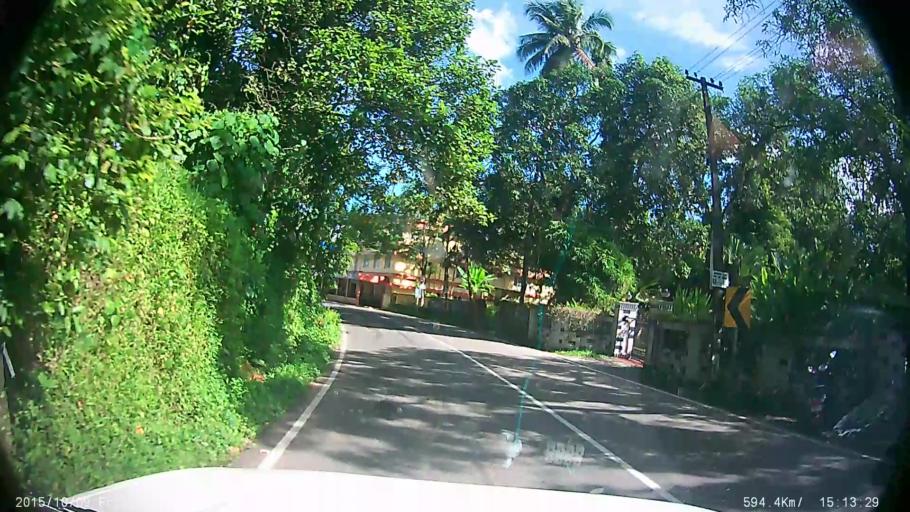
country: IN
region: Kerala
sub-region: Ernakulam
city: Piravam
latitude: 9.8653
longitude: 76.5912
